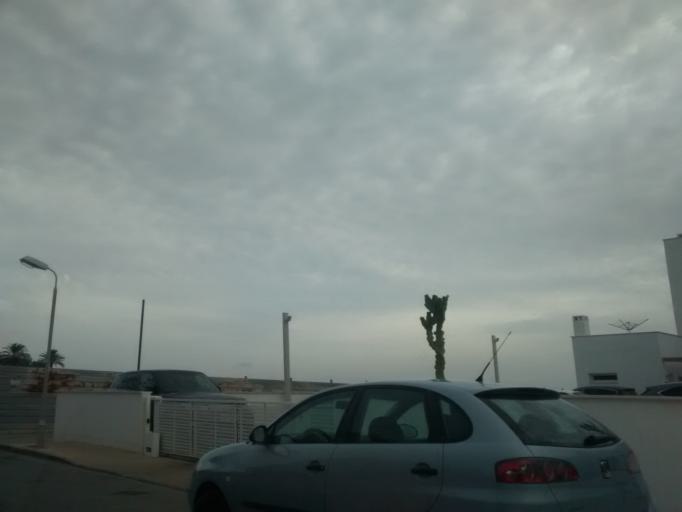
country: ES
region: Murcia
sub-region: Murcia
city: San Pedro del Pinatar
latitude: 37.7789
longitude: -0.7543
